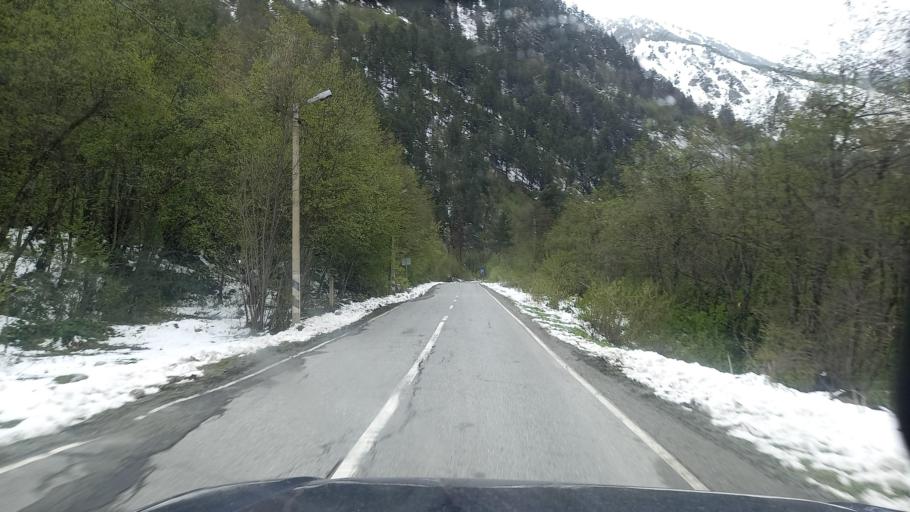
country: RU
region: North Ossetia
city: Mizur
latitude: 42.7955
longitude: 43.9251
